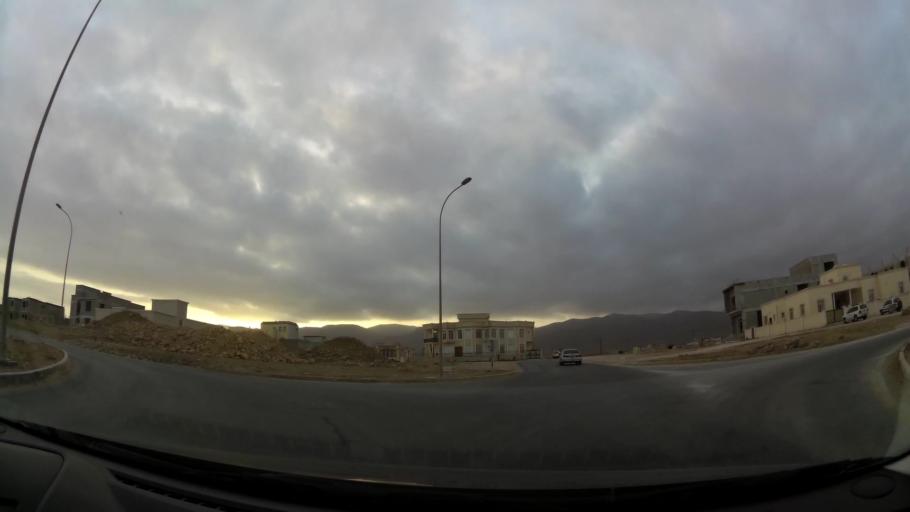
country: OM
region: Zufar
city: Salalah
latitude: 17.0406
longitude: 54.0230
